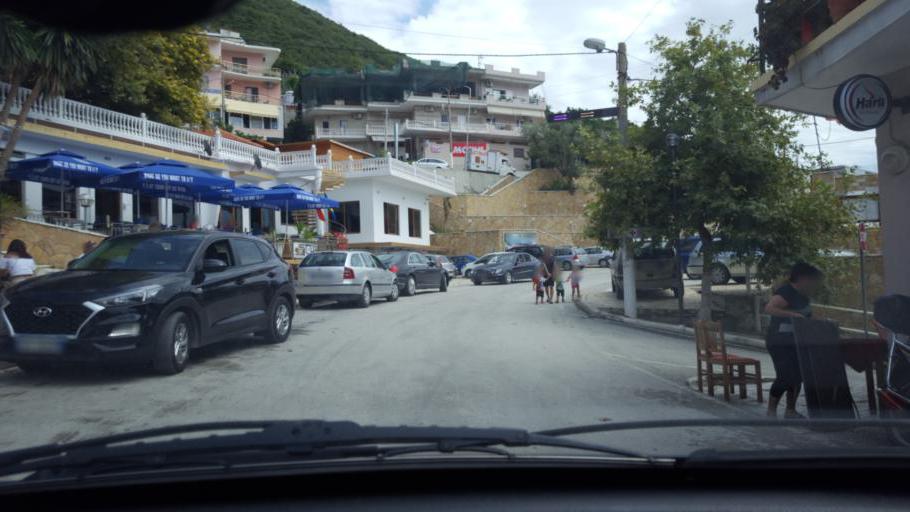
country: AL
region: Vlore
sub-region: Rrethi i Sarandes
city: Lukove
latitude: 40.0618
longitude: 19.8575
